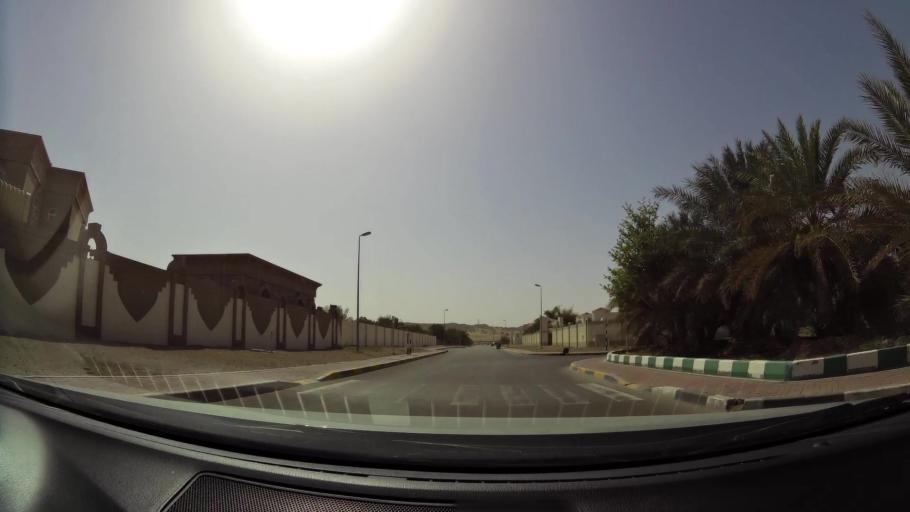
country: OM
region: Al Buraimi
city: Al Buraymi
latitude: 24.3144
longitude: 55.8074
